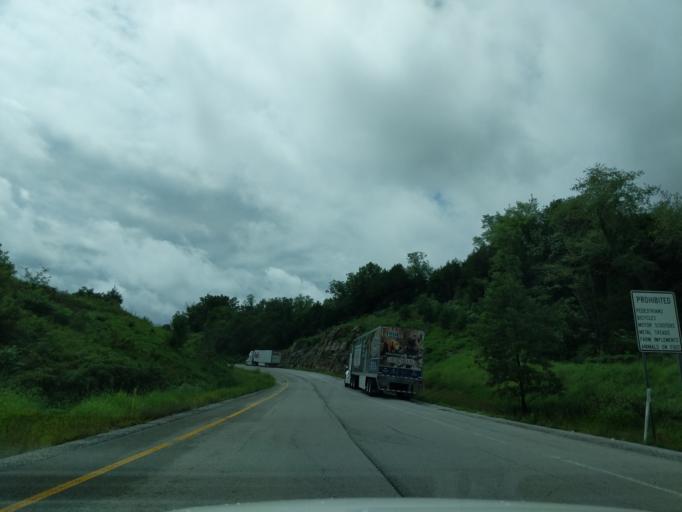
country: US
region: Kentucky
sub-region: Barren County
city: Cave City
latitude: 37.0984
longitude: -86.0553
